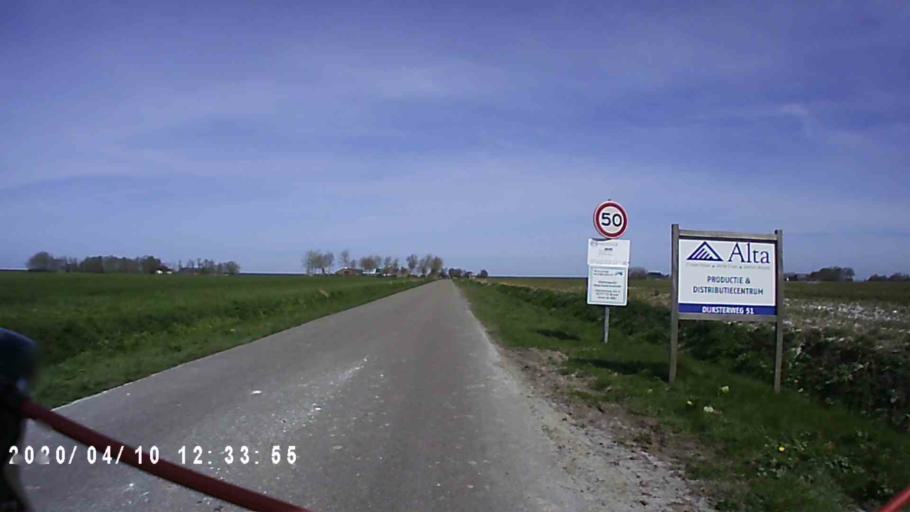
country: NL
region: Groningen
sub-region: Gemeente De Marne
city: Ulrum
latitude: 53.3953
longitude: 6.4164
